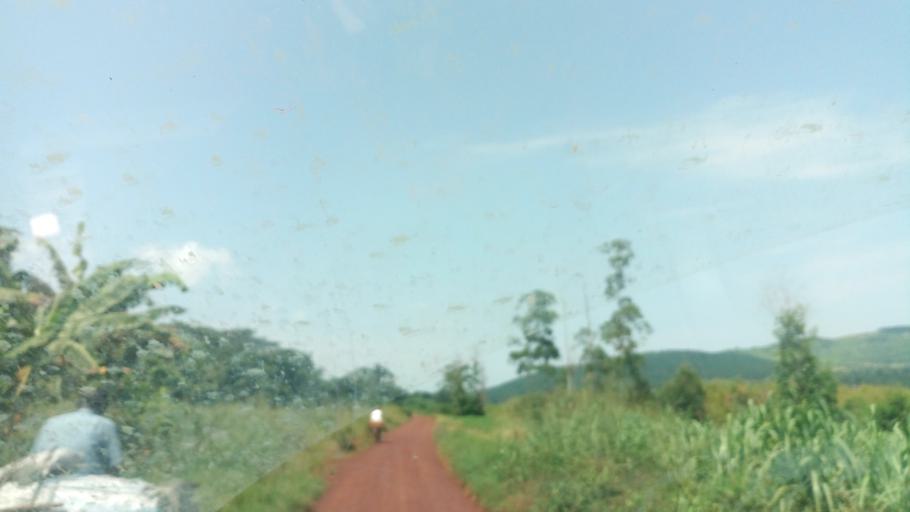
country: UG
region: Western Region
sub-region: Masindi District
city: Masindi
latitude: 1.6582
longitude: 31.8099
